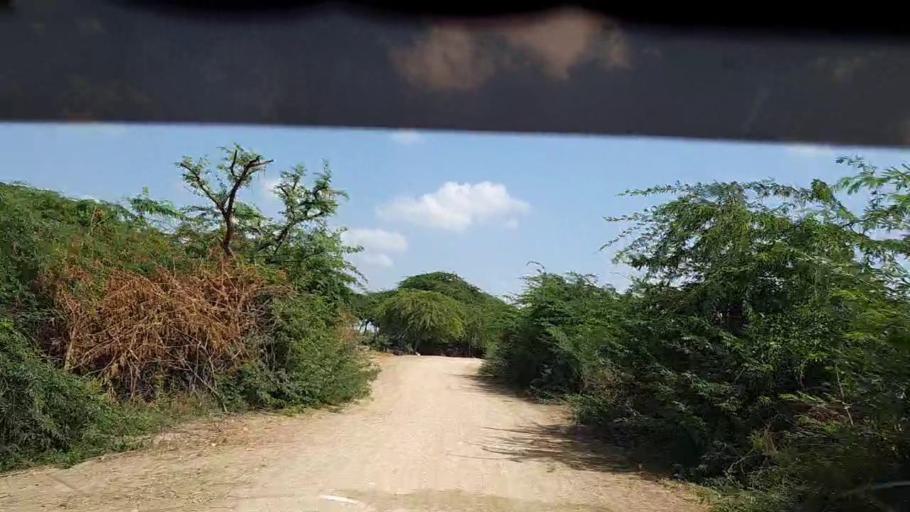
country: PK
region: Sindh
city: Kadhan
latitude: 24.5984
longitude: 68.9904
